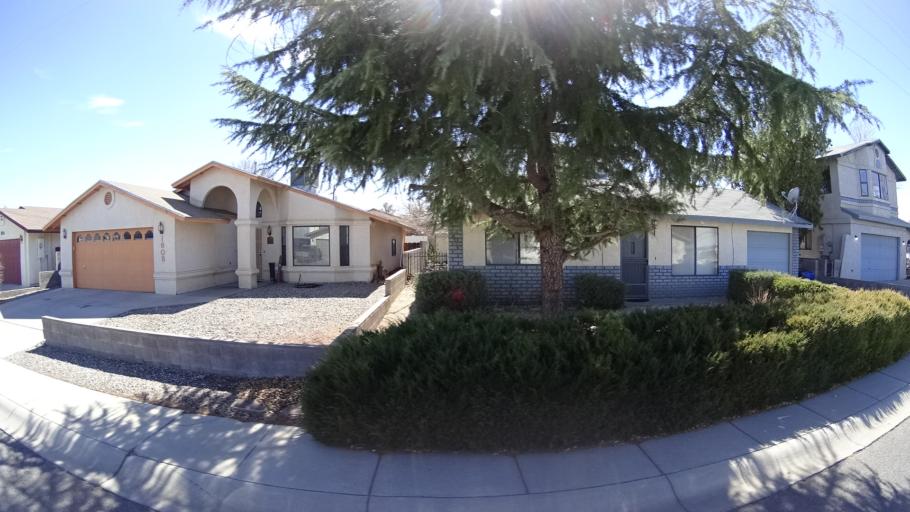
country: US
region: Arizona
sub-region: Mohave County
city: Kingman
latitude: 35.2082
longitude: -114.0376
